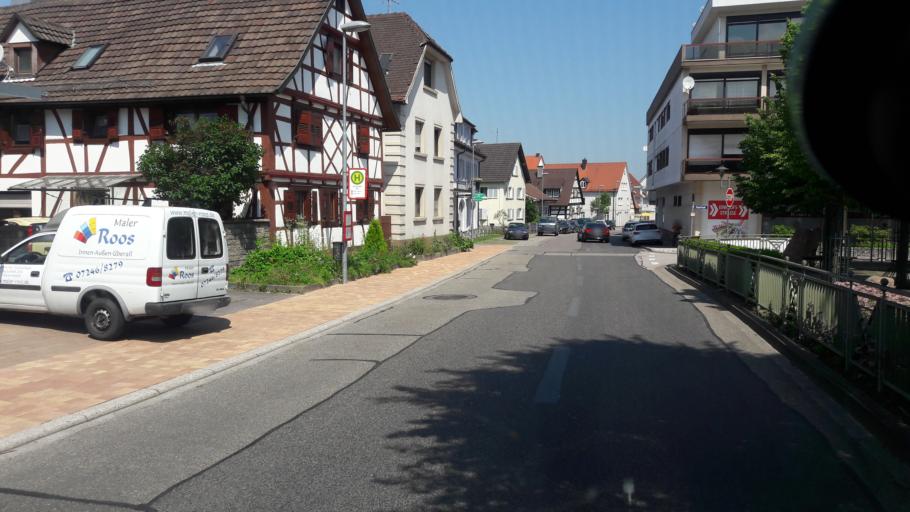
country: DE
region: Baden-Wuerttemberg
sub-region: Karlsruhe Region
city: Malsch
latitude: 48.8798
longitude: 8.3350
